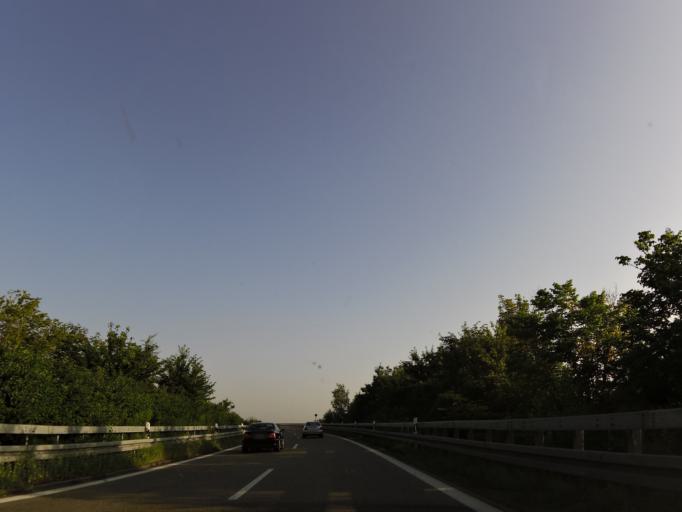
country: DE
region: Baden-Wuerttemberg
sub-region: Tuebingen Region
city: Langenau
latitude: 48.4622
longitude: 10.1175
